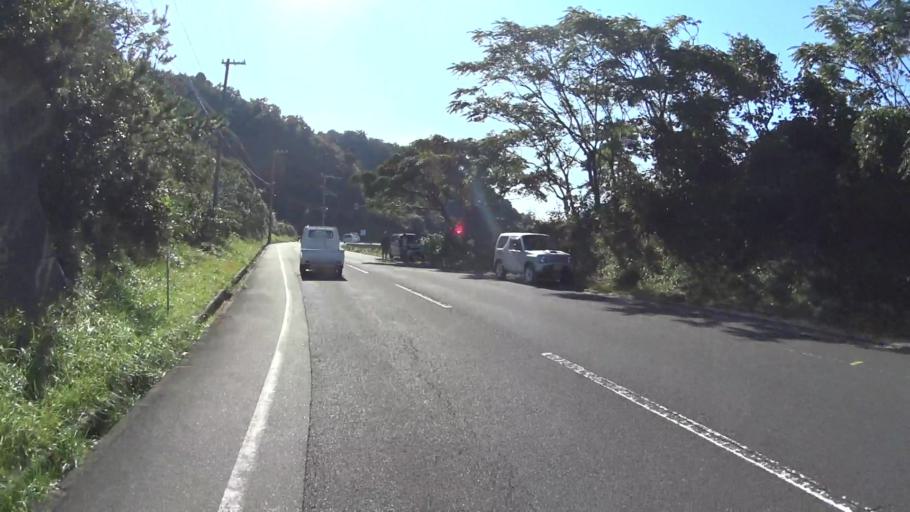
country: JP
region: Kyoto
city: Miyazu
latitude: 35.7179
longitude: 135.0714
